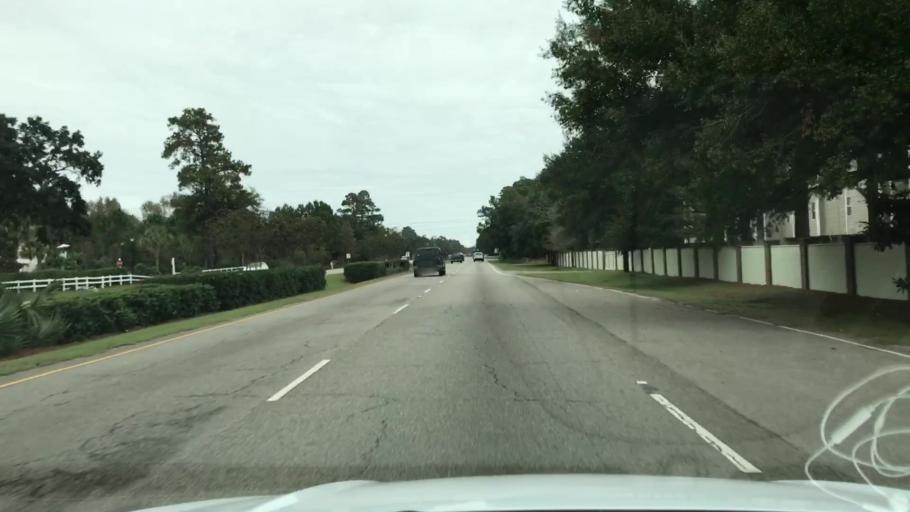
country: US
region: South Carolina
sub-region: Georgetown County
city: Murrells Inlet
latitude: 33.4656
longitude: -79.1087
